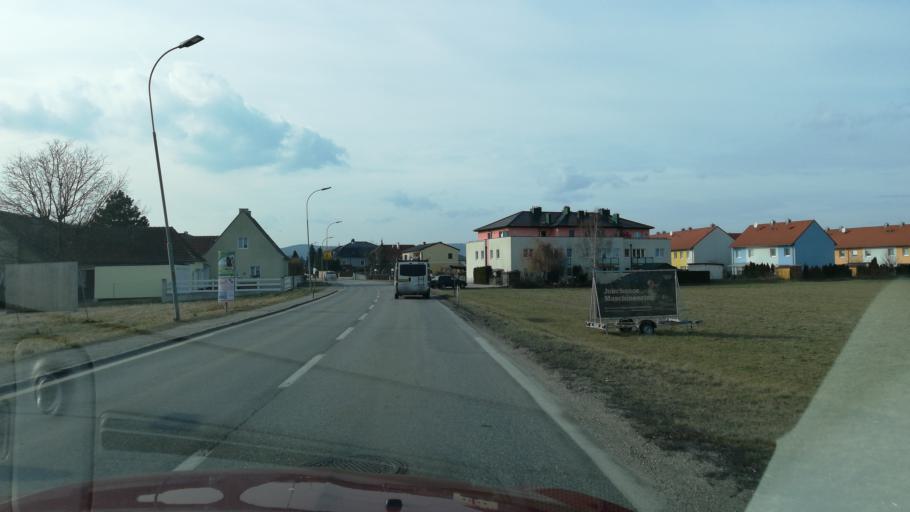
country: AT
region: Lower Austria
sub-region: Politischer Bezirk Sankt Polten
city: Traismauer
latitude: 48.3487
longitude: 15.7582
